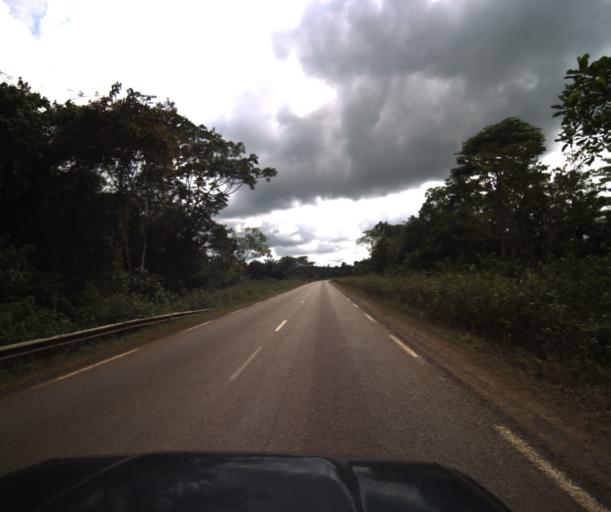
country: CM
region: Littoral
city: Edea
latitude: 3.8113
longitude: 10.3016
